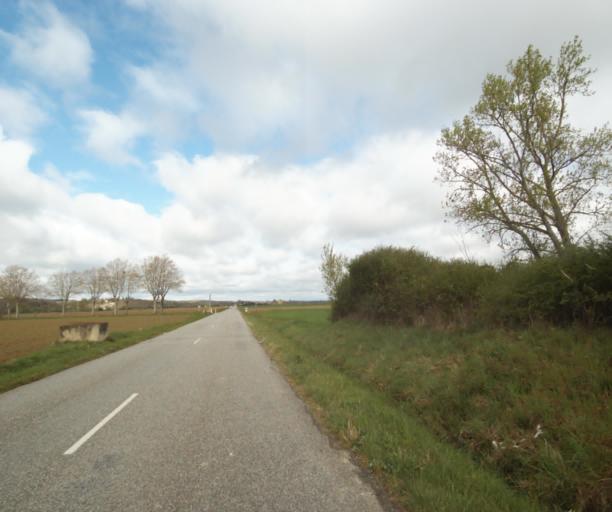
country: FR
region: Midi-Pyrenees
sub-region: Departement de l'Ariege
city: Saverdun
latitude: 43.2508
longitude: 1.5506
